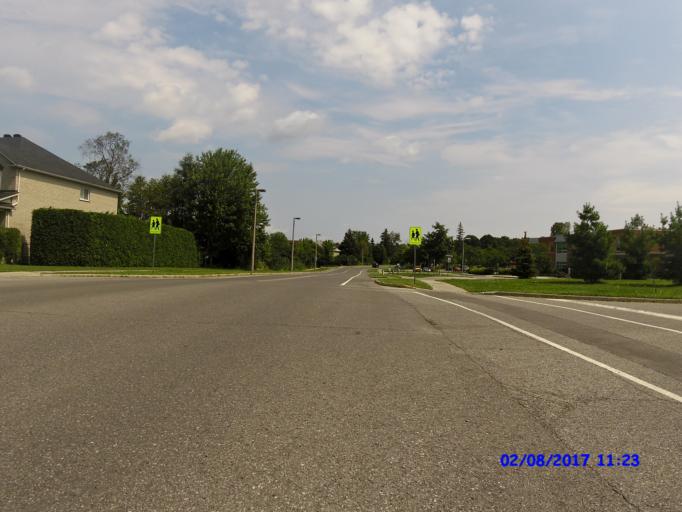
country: CA
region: Ontario
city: Bells Corners
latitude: 45.3273
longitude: -75.9241
